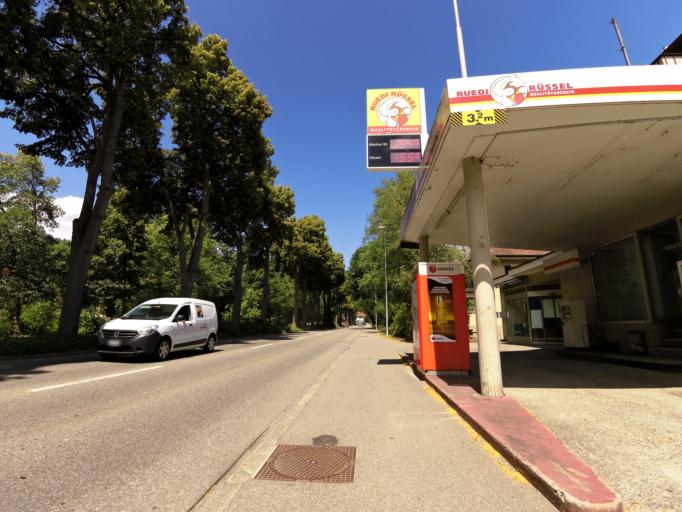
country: CH
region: Solothurn
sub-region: Bezirk Thal
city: Balsthal
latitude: 47.3109
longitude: 7.6895
